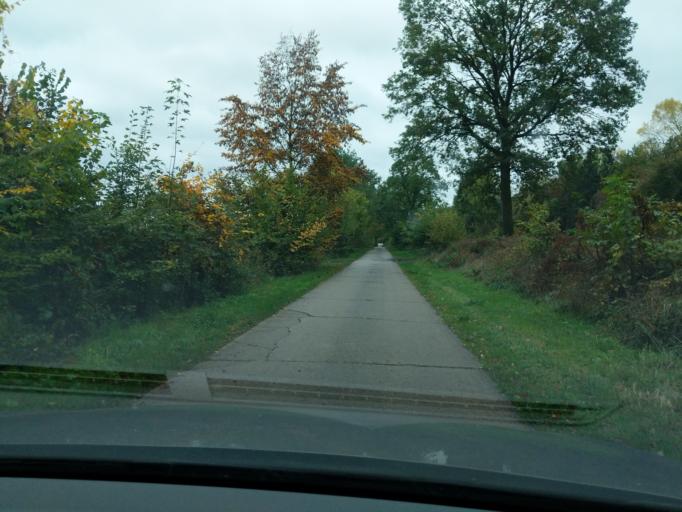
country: DE
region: Schleswig-Holstein
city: Buchhorst
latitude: 53.3920
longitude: 10.5593
